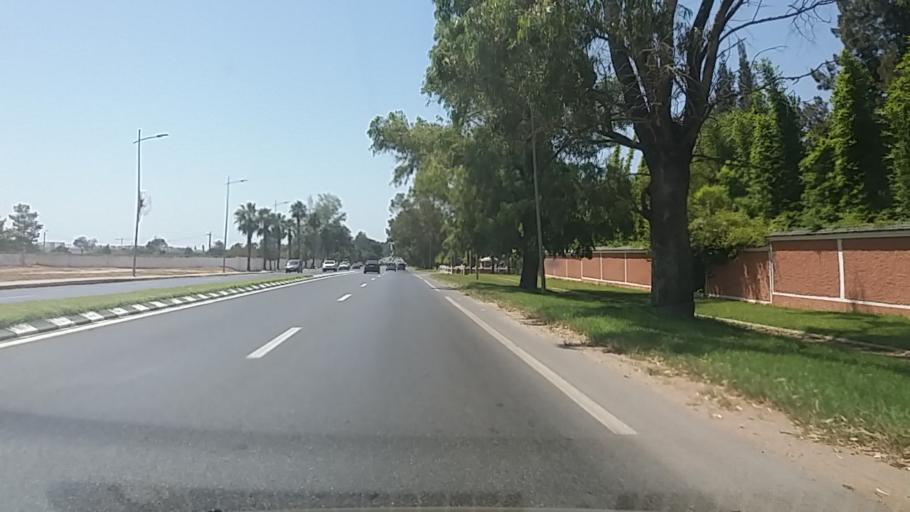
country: MA
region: Rabat-Sale-Zemmour-Zaer
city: Sale
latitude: 34.0297
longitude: -6.7416
